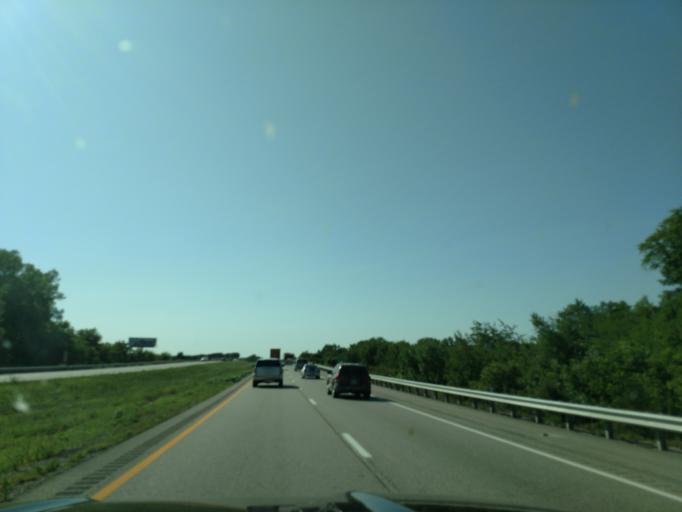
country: US
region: Missouri
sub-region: Andrew County
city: Country Club Village
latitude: 39.8691
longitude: -94.8283
